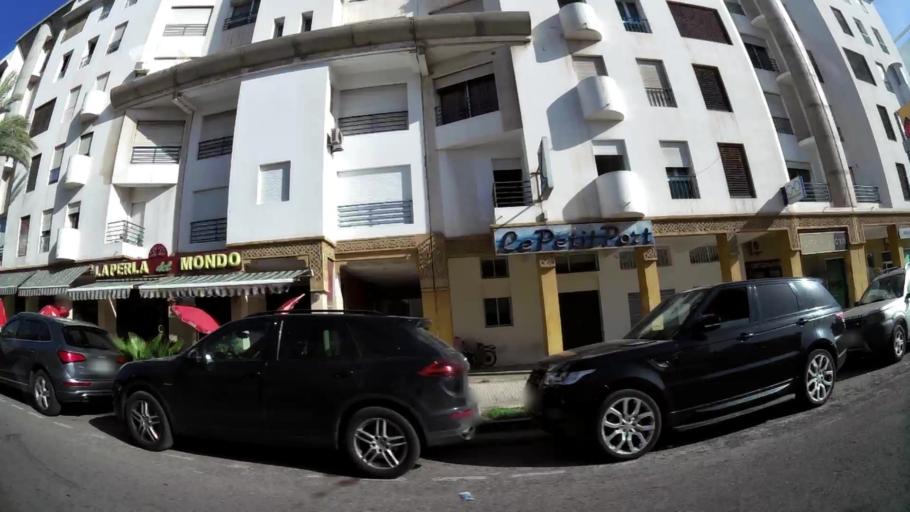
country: MA
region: Souss-Massa-Draa
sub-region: Agadir-Ida-ou-Tnan
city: Agadir
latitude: 30.4290
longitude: -9.5898
